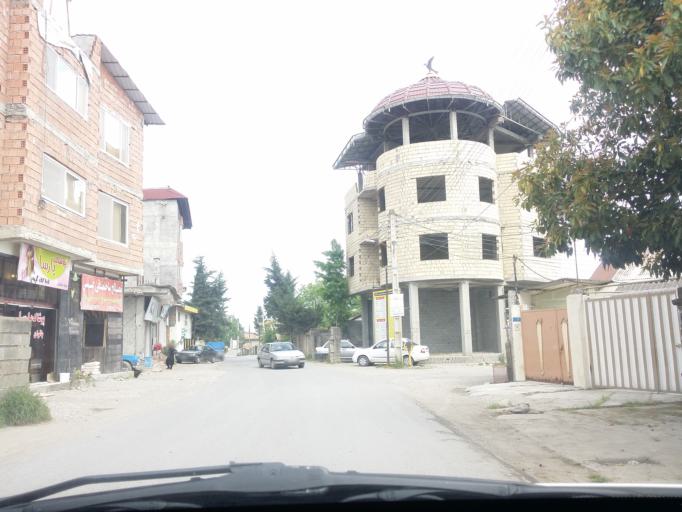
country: IR
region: Mazandaran
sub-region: Nowshahr
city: Nowshahr
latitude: 36.6239
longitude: 51.4931
